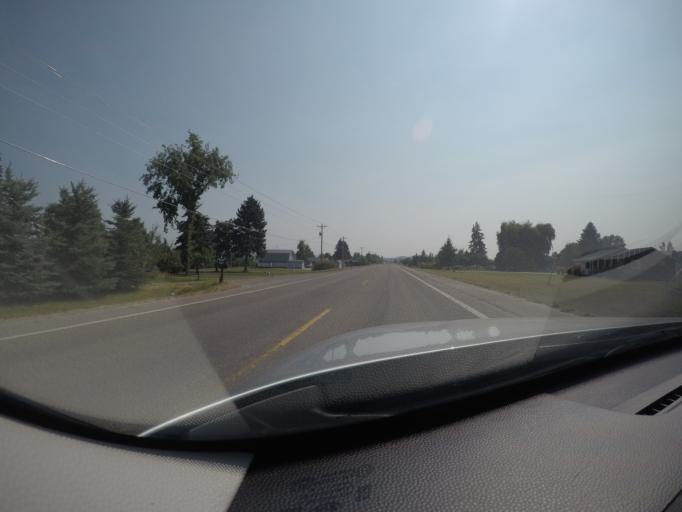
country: US
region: Montana
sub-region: Lake County
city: Polson
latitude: 47.7240
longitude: -114.1886
